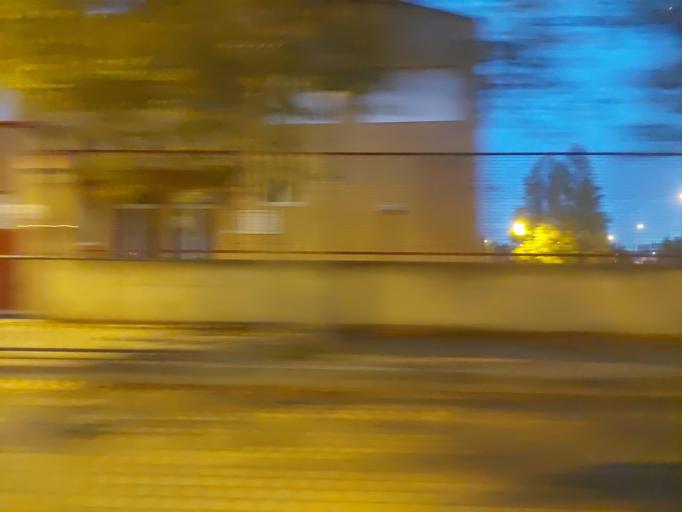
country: ES
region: Madrid
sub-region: Provincia de Madrid
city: Leganes
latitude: 40.3195
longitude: -3.7504
